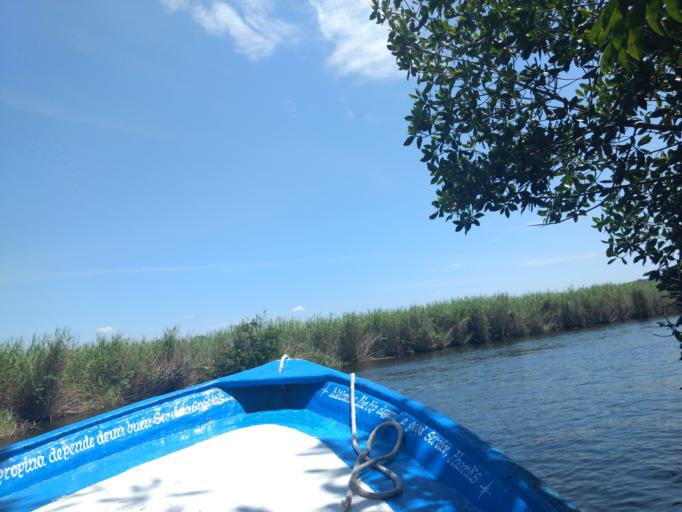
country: MX
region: Nayarit
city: San Blas
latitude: 21.5362
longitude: -105.2371
